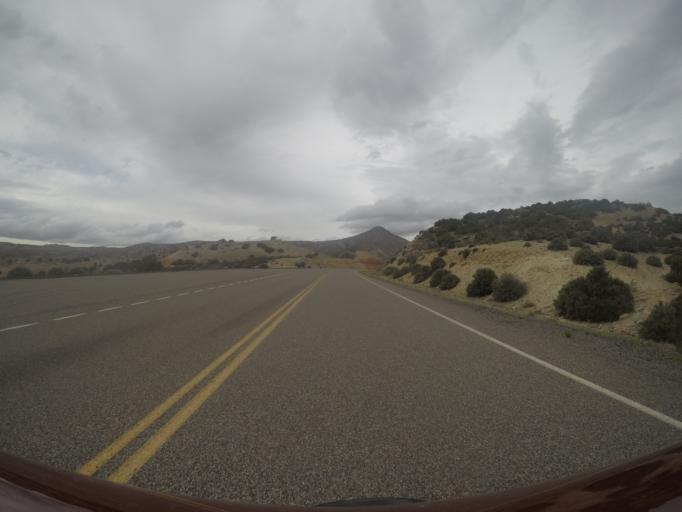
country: US
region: Wyoming
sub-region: Big Horn County
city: Lovell
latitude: 45.0090
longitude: -108.2688
